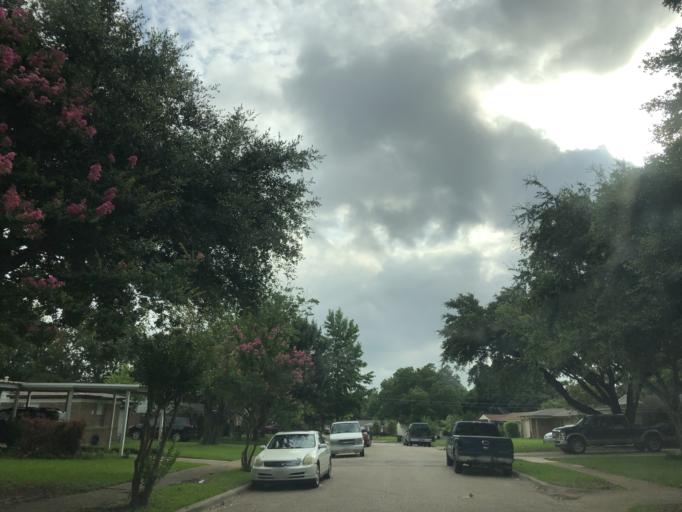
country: US
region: Texas
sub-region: Dallas County
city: Garland
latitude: 32.8325
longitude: -96.6461
